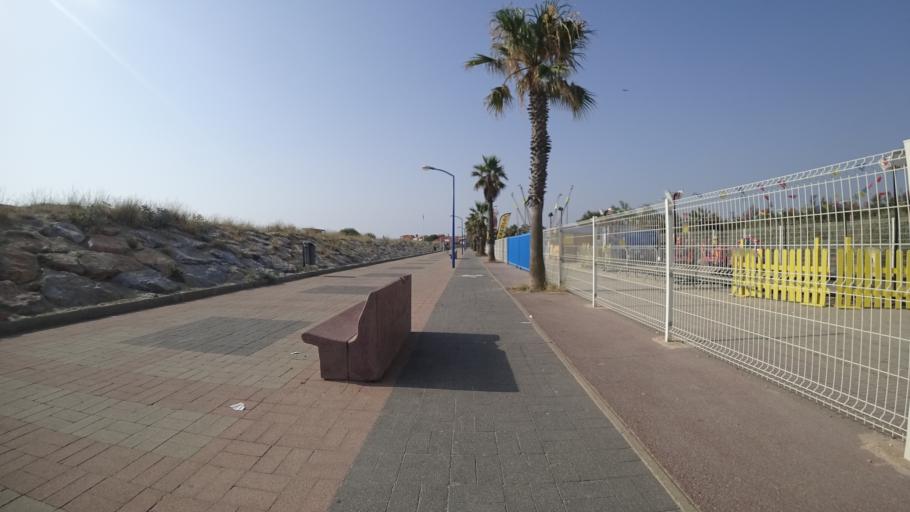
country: FR
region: Languedoc-Roussillon
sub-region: Departement des Pyrenees-Orientales
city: Sainte-Marie-Plage
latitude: 42.7316
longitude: 3.0372
